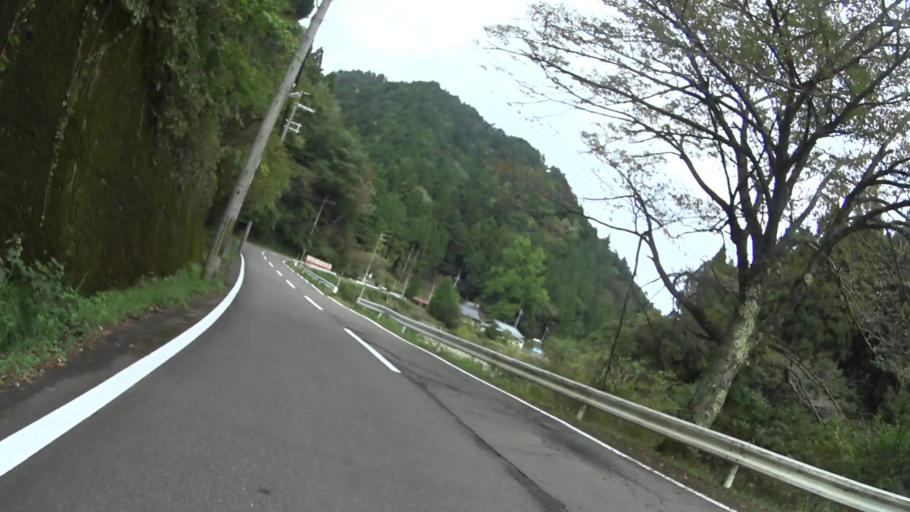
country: JP
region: Shiga Prefecture
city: Kitahama
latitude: 35.2179
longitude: 135.7775
